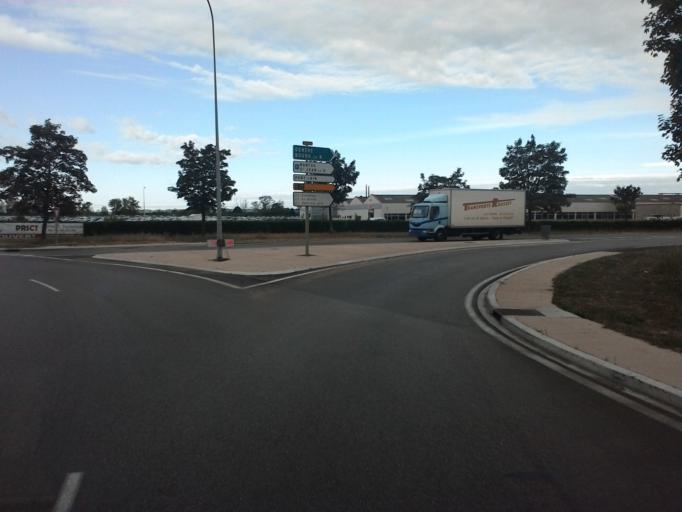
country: FR
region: Rhone-Alpes
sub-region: Departement de l'Ain
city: Amberieu-en-Bugey
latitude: 45.9832
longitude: 5.3477
